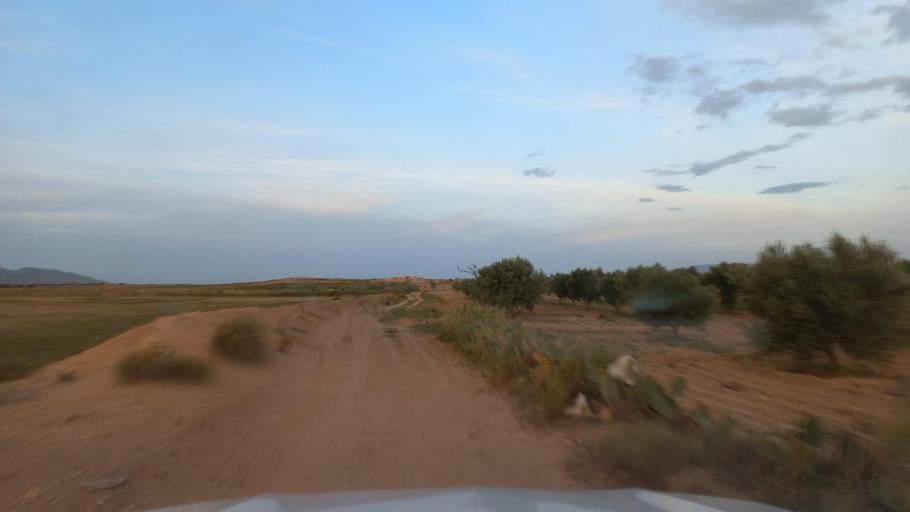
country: TN
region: Al Qasrayn
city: Sbiba
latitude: 35.3516
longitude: 9.0261
